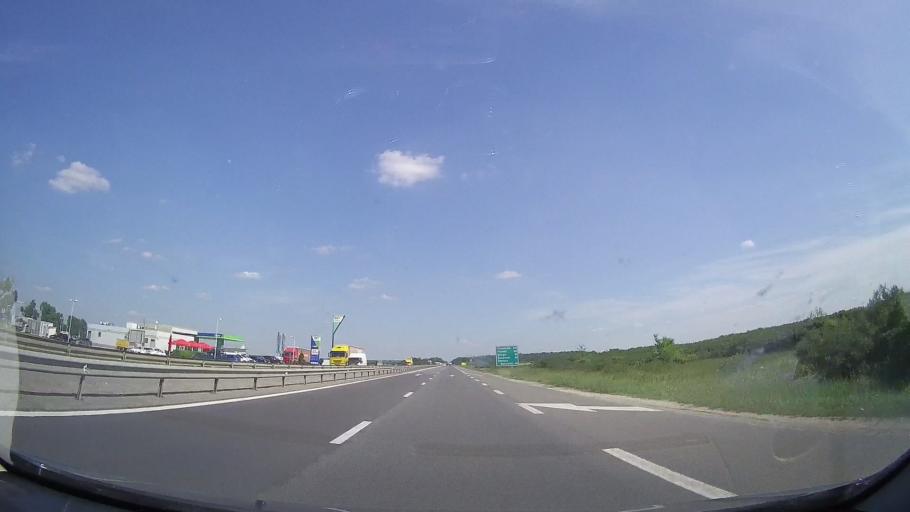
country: RO
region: Dambovita
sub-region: Comuna Corbii Mari
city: Corbii Mari
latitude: 44.5329
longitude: 25.5314
